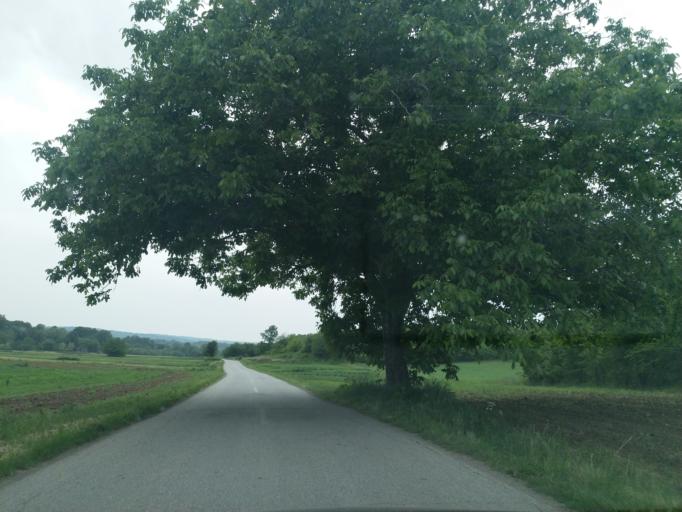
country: RS
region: Central Serbia
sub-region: Pomoravski Okrug
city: Paracin
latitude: 43.8751
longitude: 21.5503
